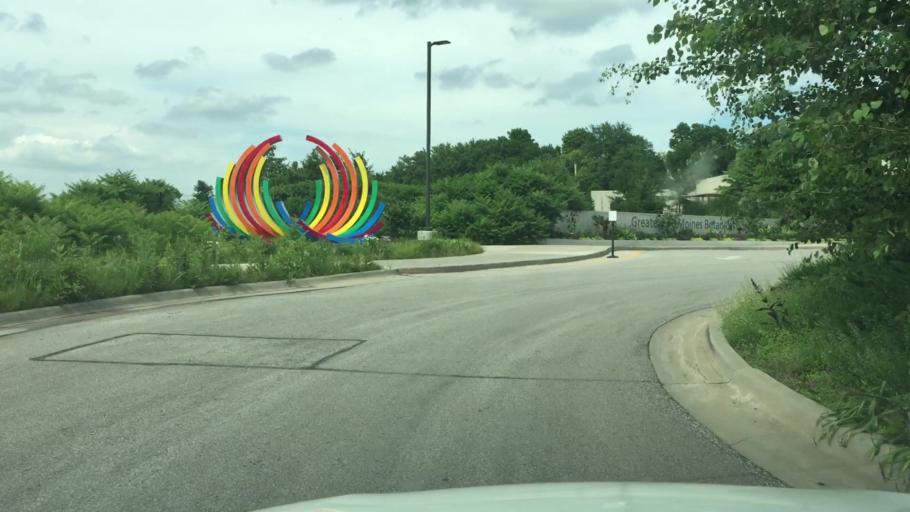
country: US
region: Iowa
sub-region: Polk County
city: Des Moines
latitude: 41.5965
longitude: -93.6151
